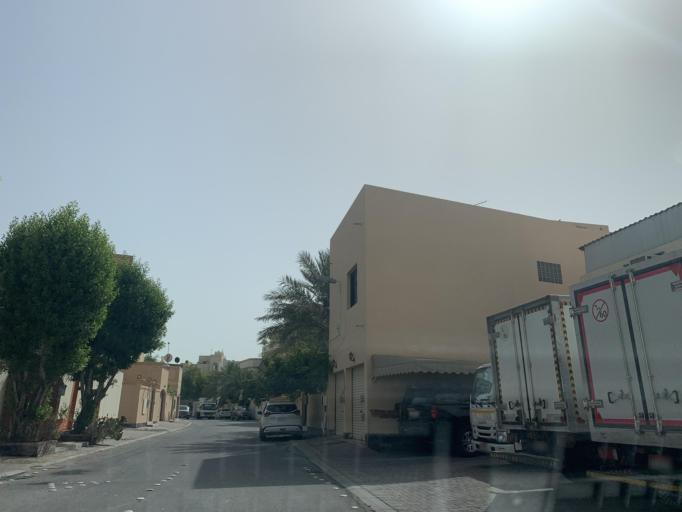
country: BH
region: Northern
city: Sitrah
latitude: 26.1323
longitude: 50.5979
